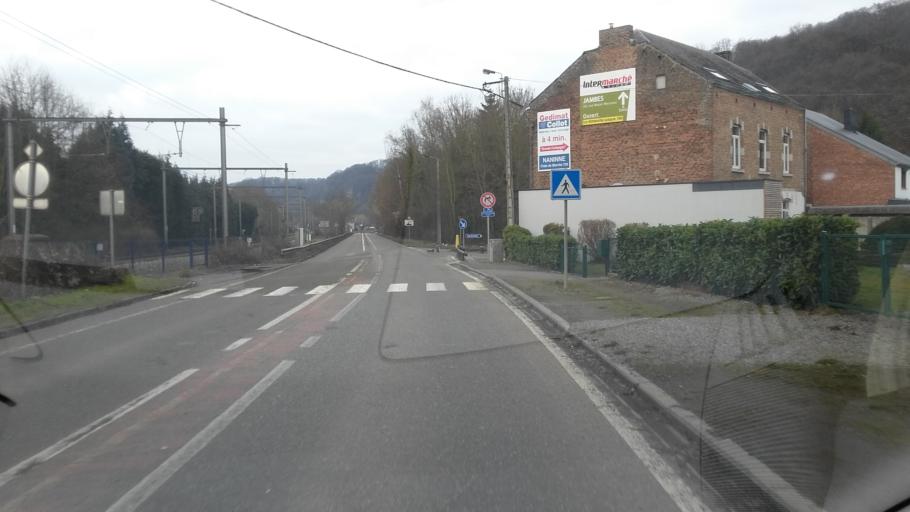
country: BE
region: Wallonia
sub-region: Province de Namur
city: Profondeville
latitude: 50.4157
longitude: 4.8874
